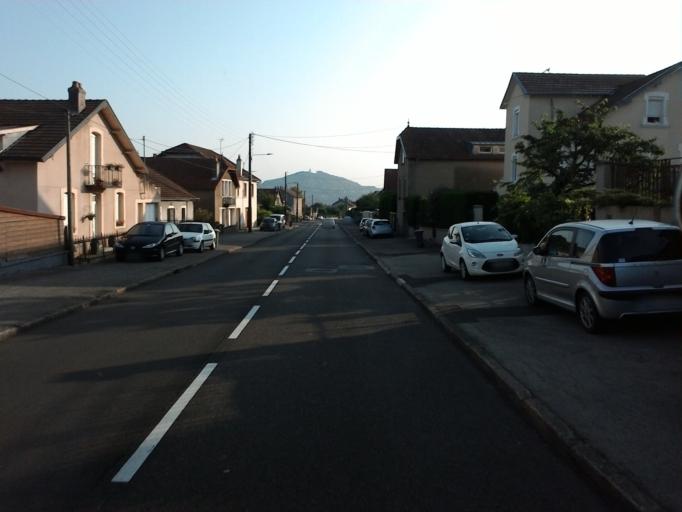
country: FR
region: Franche-Comte
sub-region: Departement de la Haute-Saone
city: Echenoz-la-Meline
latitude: 47.6057
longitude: 6.1428
